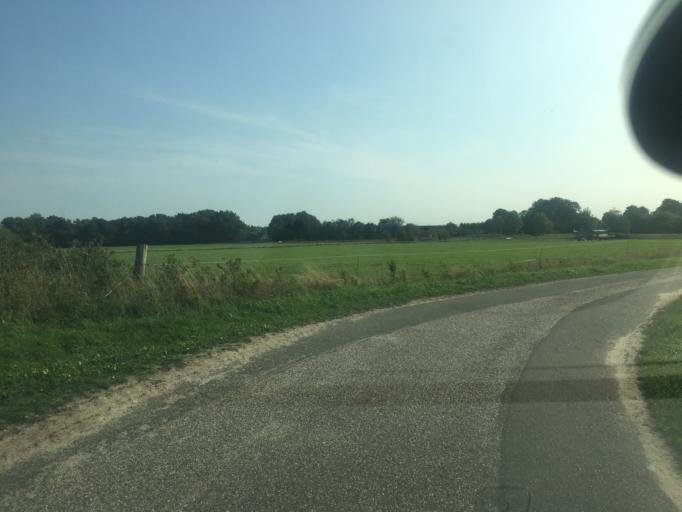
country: DK
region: South Denmark
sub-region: Tonder Kommune
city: Tonder
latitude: 54.9621
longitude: 8.9011
